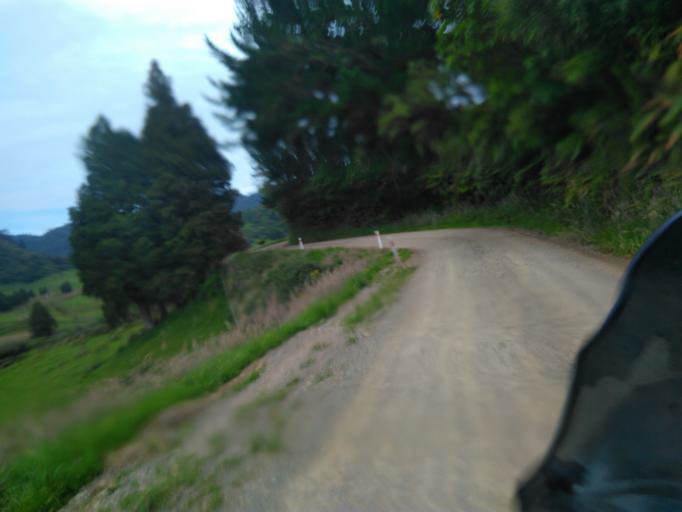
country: NZ
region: Bay of Plenty
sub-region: Opotiki District
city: Opotiki
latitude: -38.1051
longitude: 177.4976
